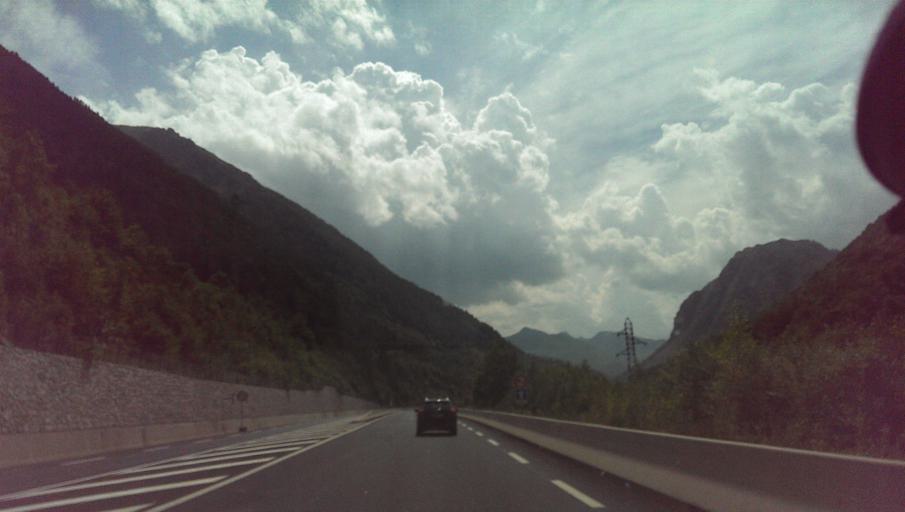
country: AD
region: Encamp
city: Pas de la Casa
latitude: 42.6029
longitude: 1.8123
